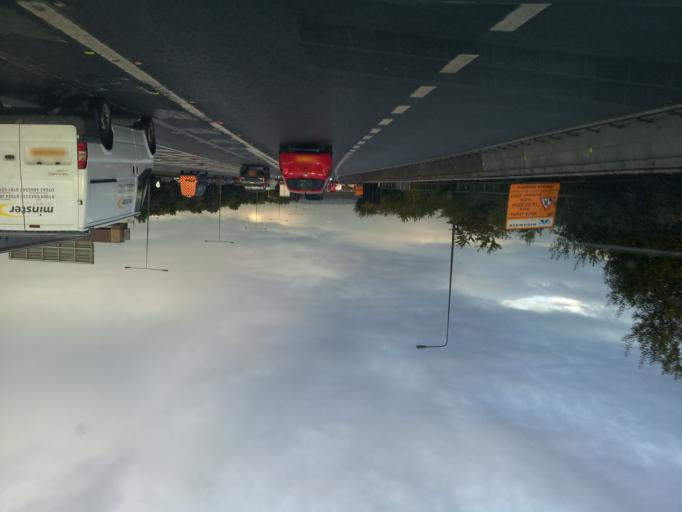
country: GB
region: England
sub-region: Borough of Bury
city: Prestwich
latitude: 53.5517
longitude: -2.2570
